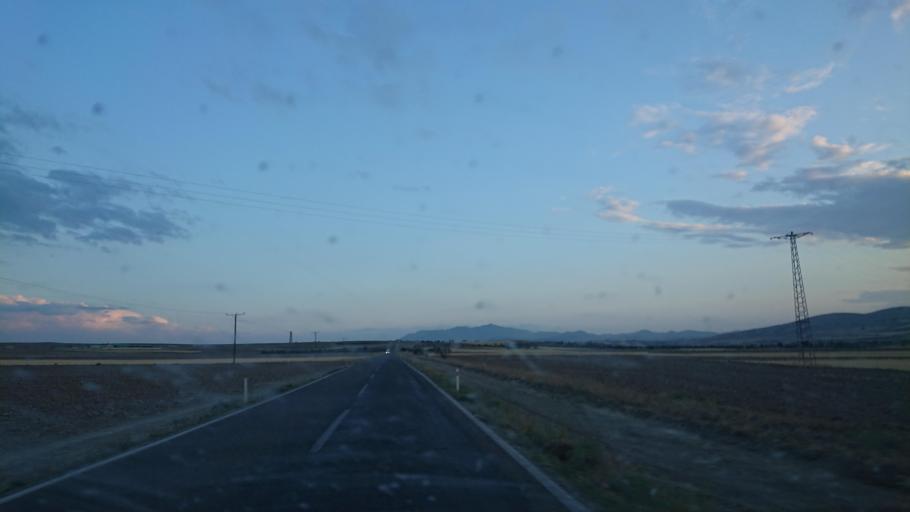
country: TR
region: Aksaray
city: Balci
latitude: 38.8117
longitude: 34.1328
